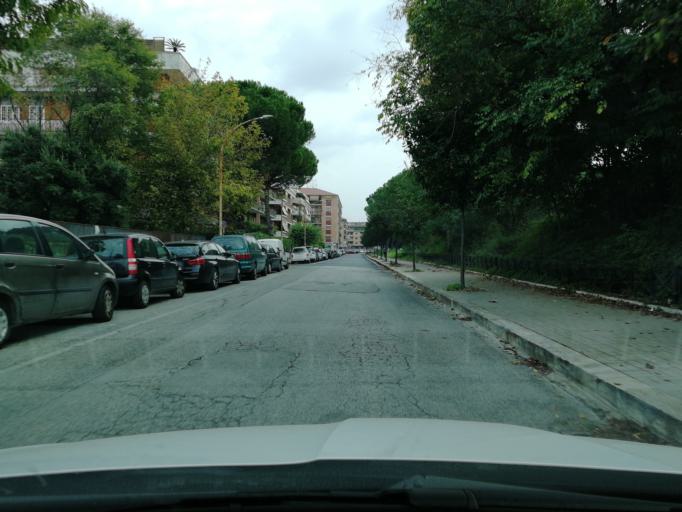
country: IT
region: Latium
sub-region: Citta metropolitana di Roma Capitale
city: Rome
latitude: 41.8546
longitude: 12.5558
